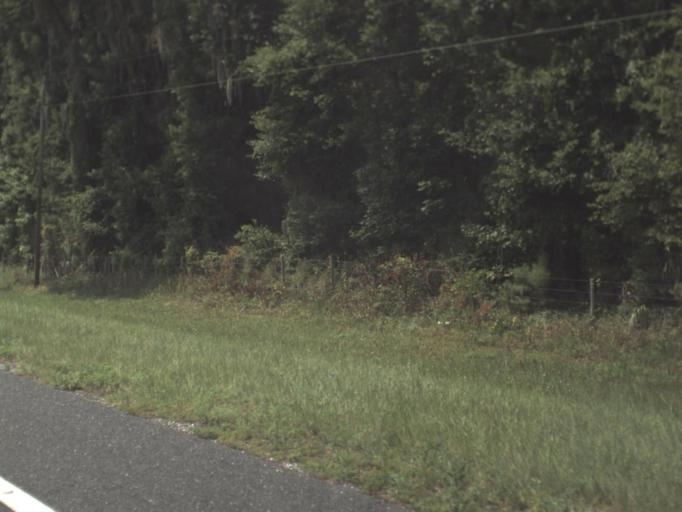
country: US
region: Florida
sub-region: Levy County
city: Chiefland
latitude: 29.4612
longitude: -82.8506
